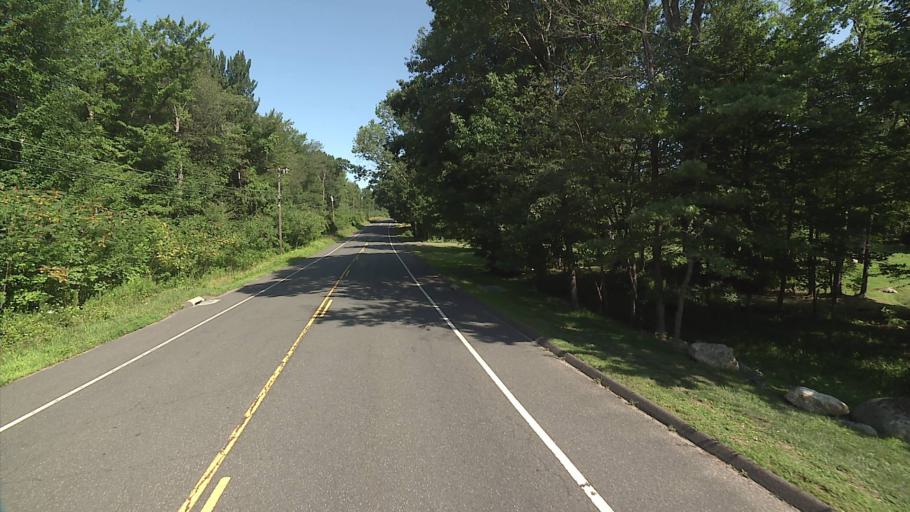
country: US
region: Connecticut
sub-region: Hartford County
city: North Granby
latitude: 41.9905
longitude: -72.8969
